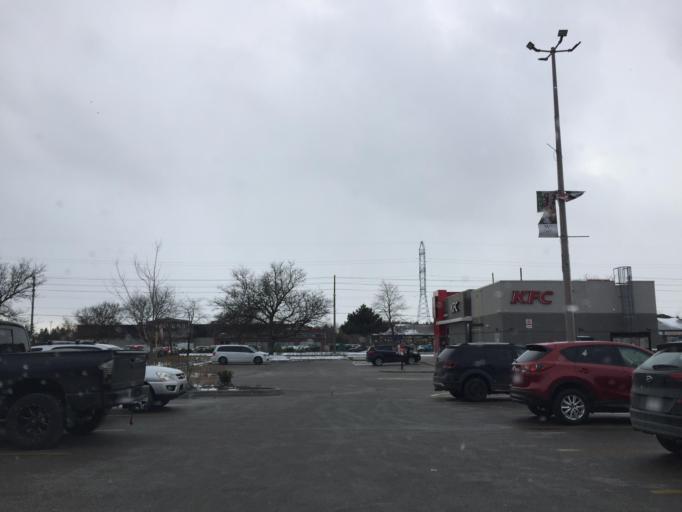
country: CA
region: Ontario
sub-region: Wellington County
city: Guelph
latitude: 43.5411
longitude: -80.2806
